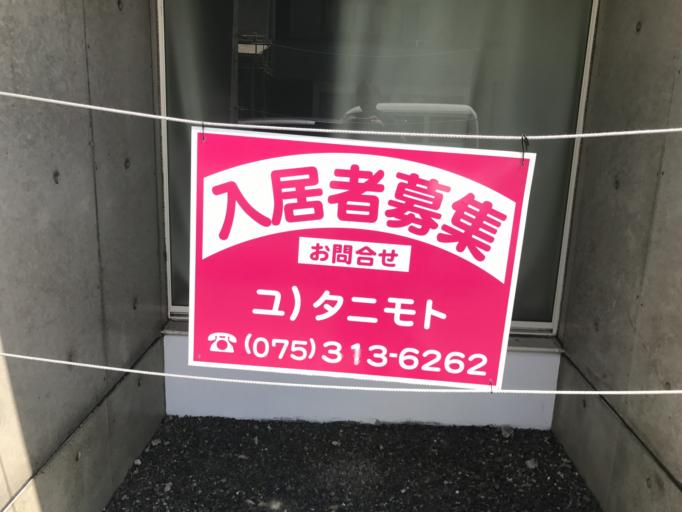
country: JP
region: Kyoto
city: Kyoto
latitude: 34.9950
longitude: 135.7360
